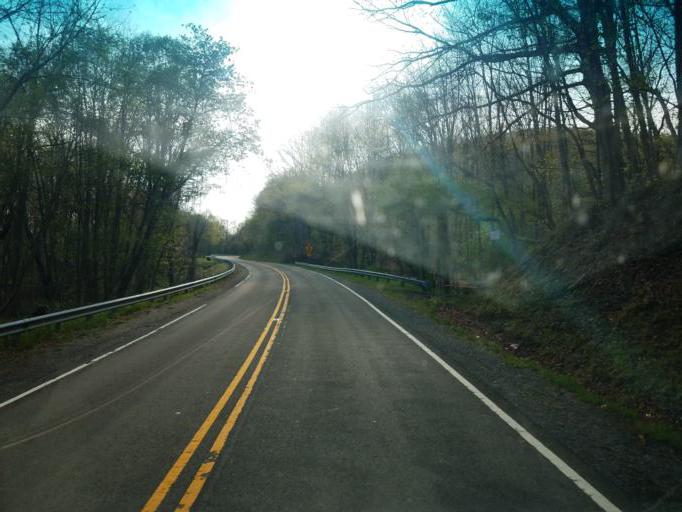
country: US
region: Virginia
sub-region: Smyth County
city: Atkins
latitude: 36.8174
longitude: -81.4363
